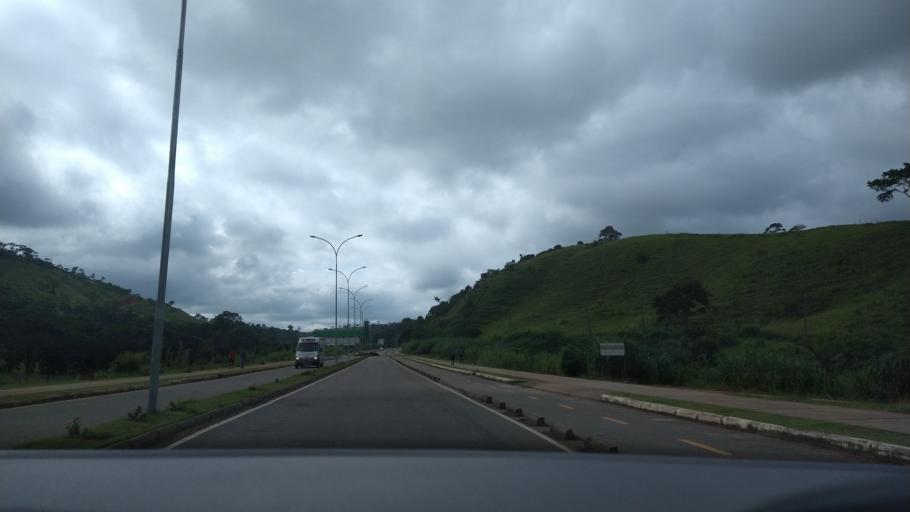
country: BR
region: Minas Gerais
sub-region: Vicosa
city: Vicosa
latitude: -20.7702
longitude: -42.8578
